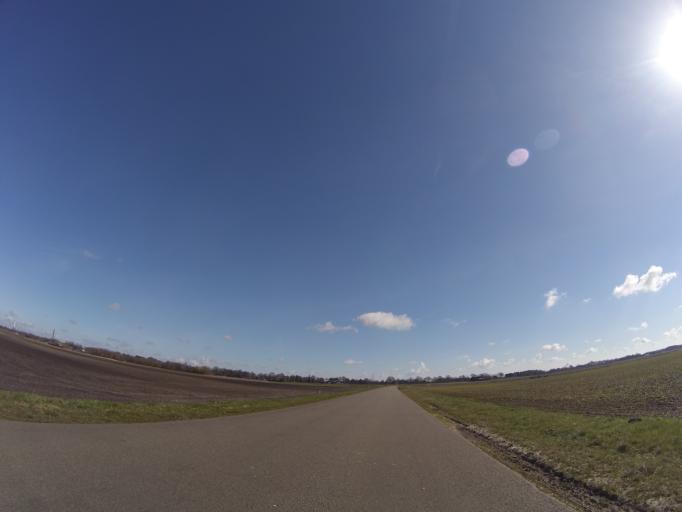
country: NL
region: Drenthe
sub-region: Gemeente Emmen
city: Klazienaveen
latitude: 52.7336
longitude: 6.9388
